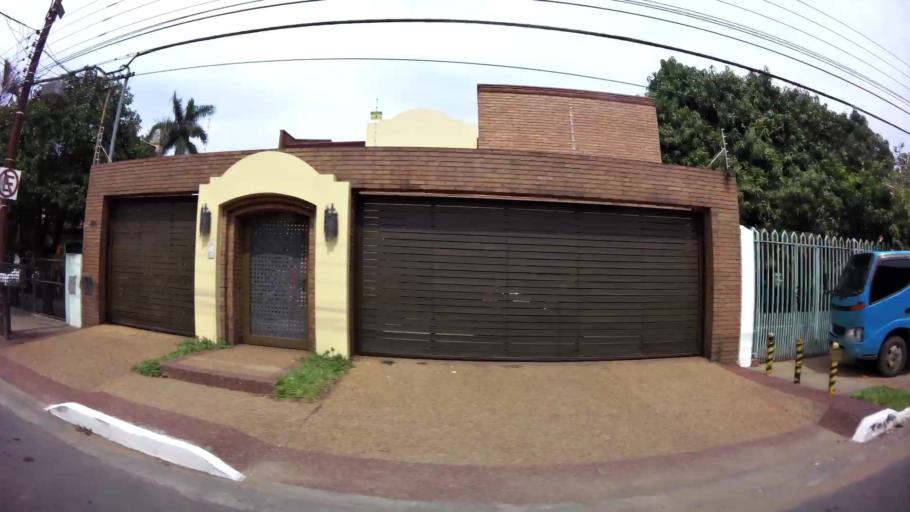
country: PY
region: Asuncion
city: Asuncion
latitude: -25.2729
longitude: -57.5633
